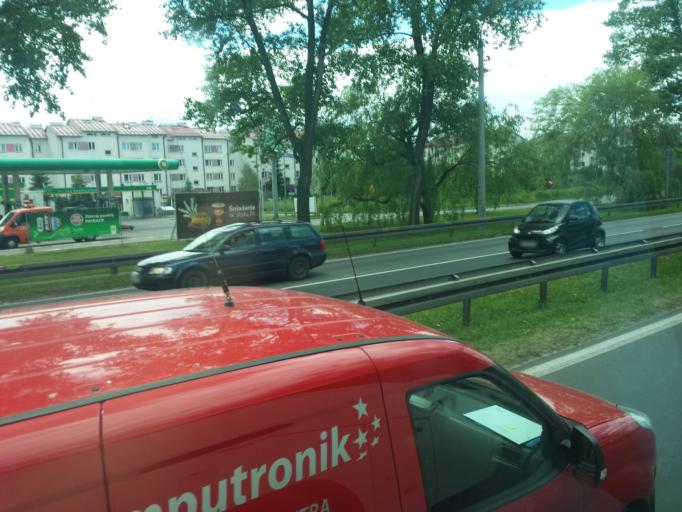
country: PL
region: Masovian Voivodeship
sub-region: Warszawa
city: Wesola
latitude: 52.2235
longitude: 21.2298
